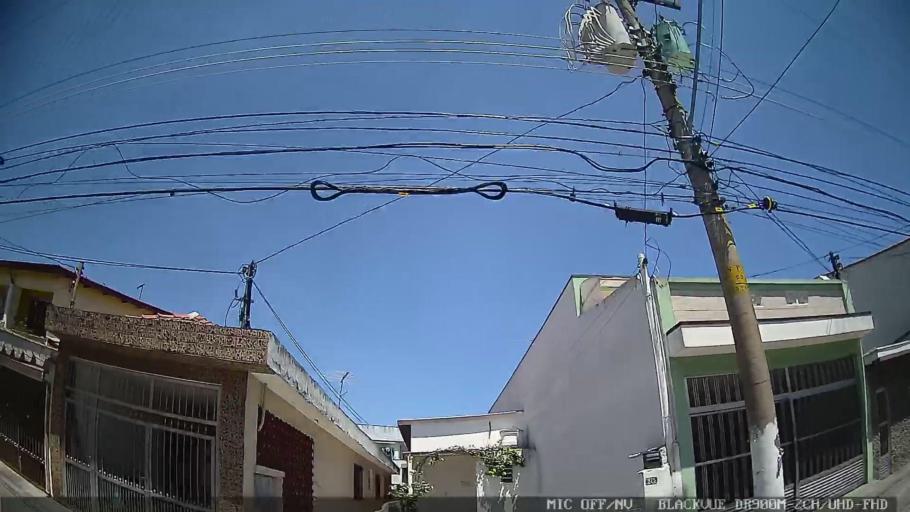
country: BR
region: Sao Paulo
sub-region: Sao Caetano Do Sul
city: Sao Caetano do Sul
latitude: -23.6051
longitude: -46.5649
